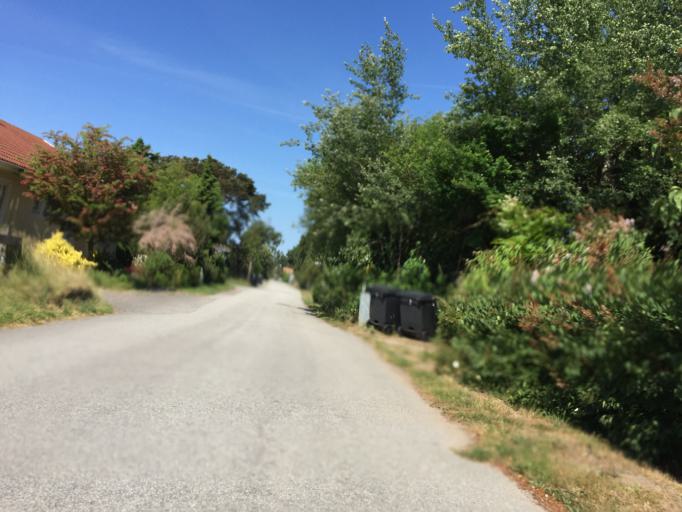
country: SE
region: Skane
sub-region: Trelleborgs Kommun
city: Anderslov
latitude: 55.3474
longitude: 13.2712
